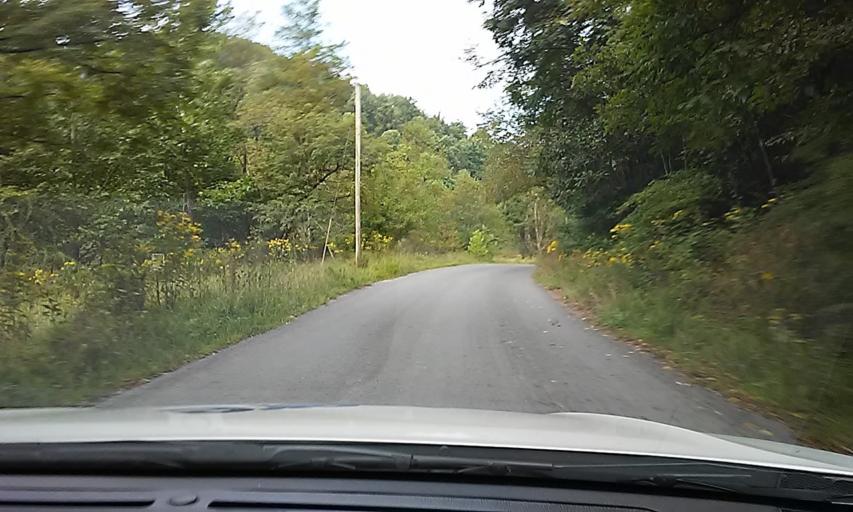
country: US
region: West Virginia
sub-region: Marion County
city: Mannington
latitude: 39.6151
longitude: -80.3420
